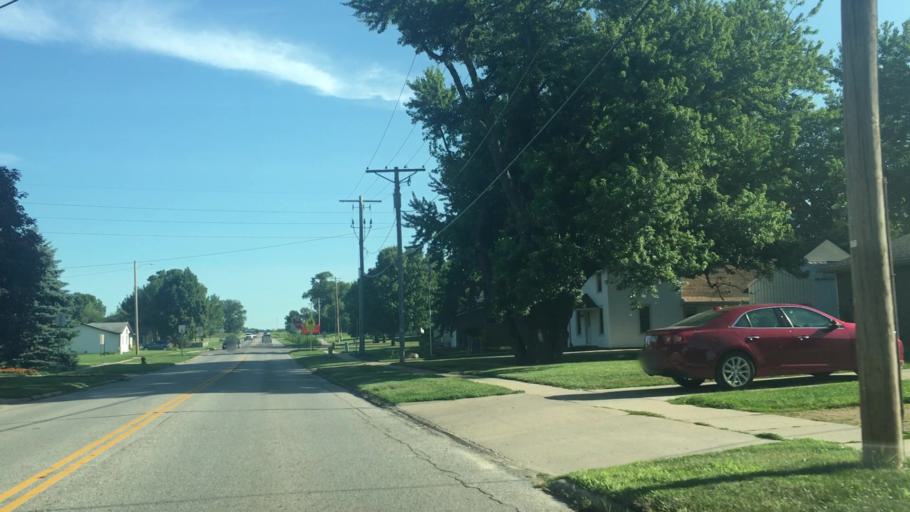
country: US
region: Iowa
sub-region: Johnson County
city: North Liberty
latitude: 41.7511
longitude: -91.5980
